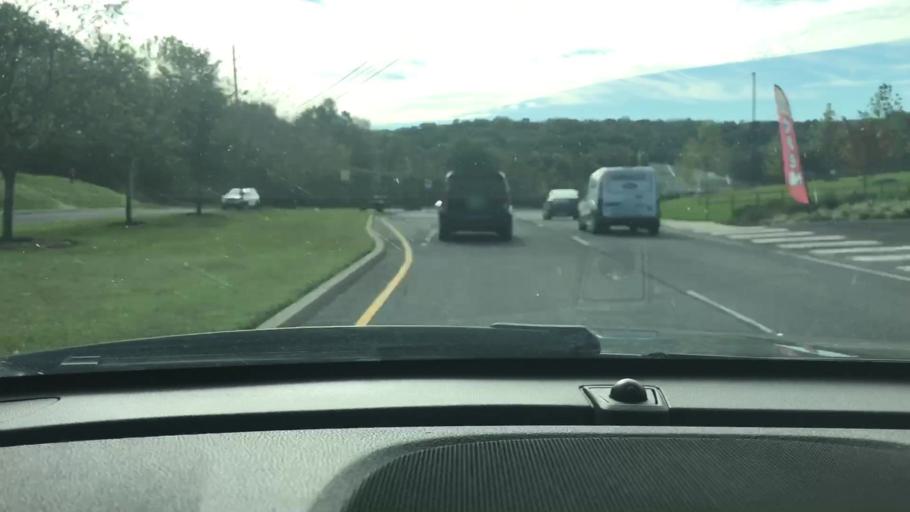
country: US
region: Tennessee
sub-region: Davidson County
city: Goodlettsville
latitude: 36.3166
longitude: -86.6998
